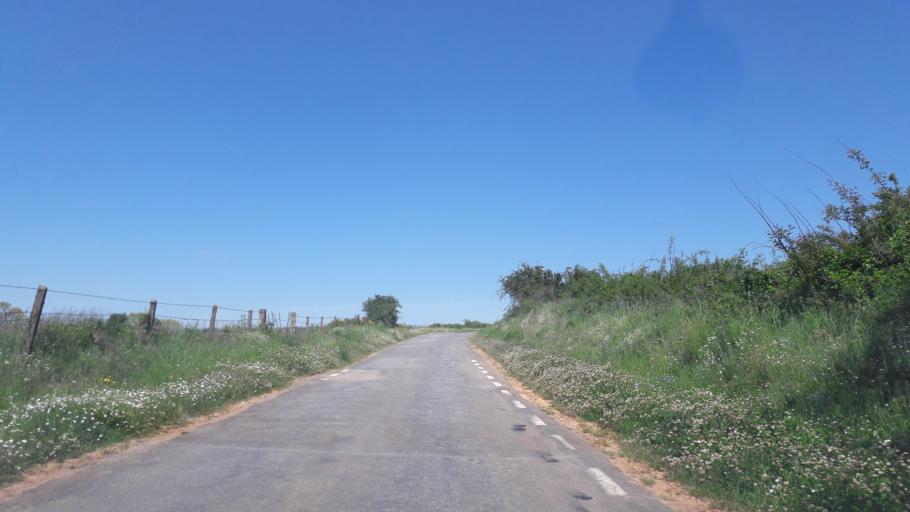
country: ES
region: Castille and Leon
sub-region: Provincia de Salamanca
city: Endrinal
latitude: 40.5777
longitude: -5.8067
